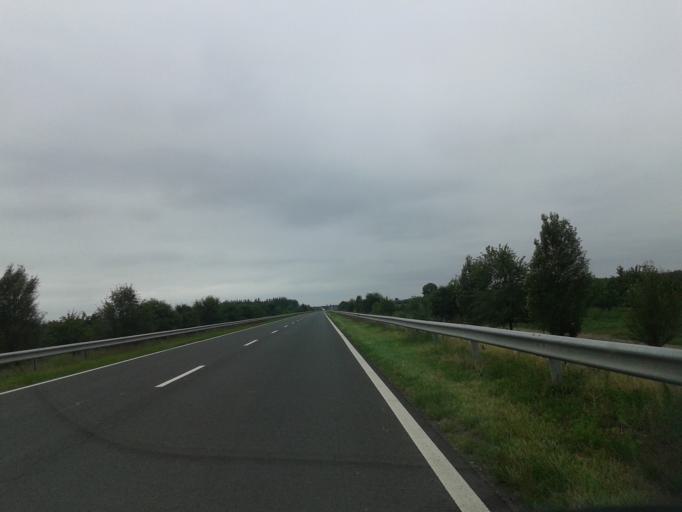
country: HU
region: Bacs-Kiskun
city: Dunavecse
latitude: 46.9237
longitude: 18.9899
